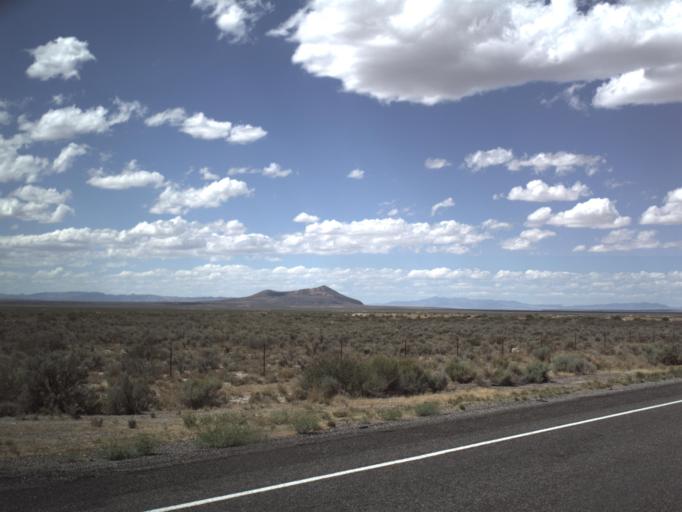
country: US
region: Utah
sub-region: Millard County
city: Fillmore
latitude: 39.1463
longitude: -112.3881
